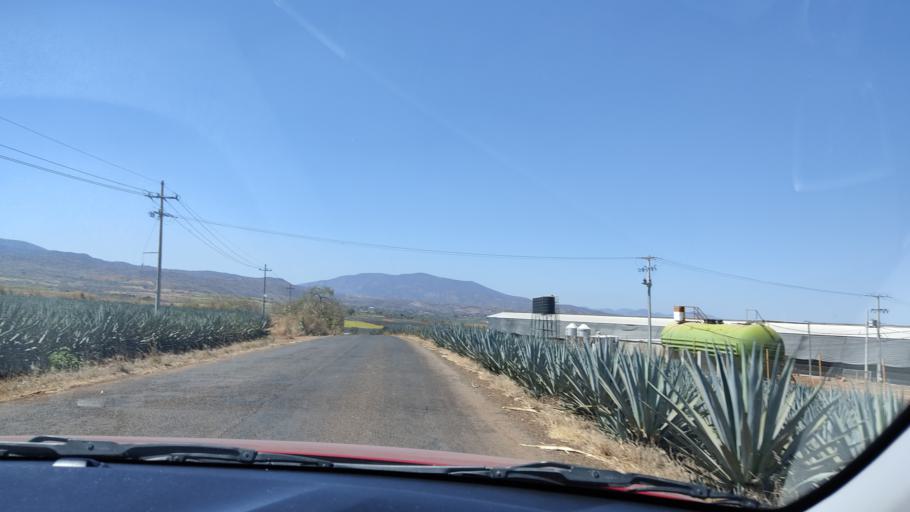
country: MX
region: Nayarit
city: Santa Maria del Oro
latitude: 21.4388
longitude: -104.6229
